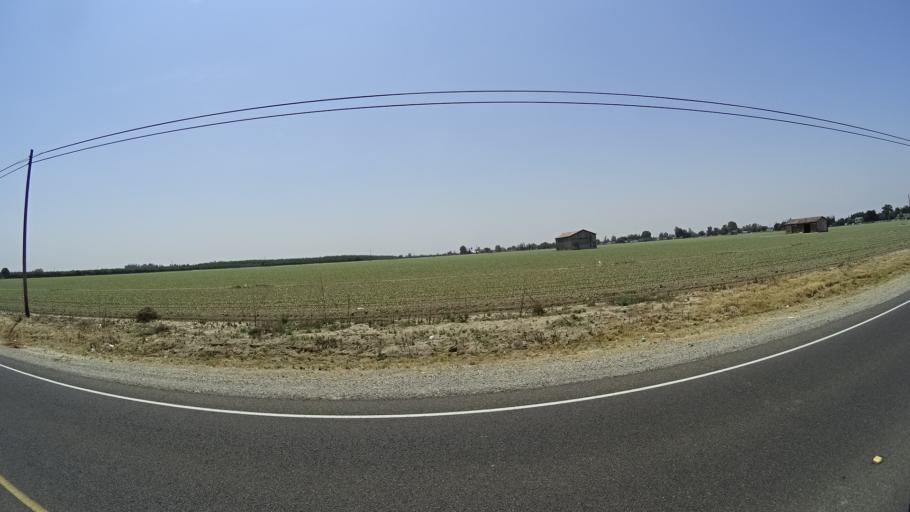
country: US
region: California
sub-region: Kings County
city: Lemoore
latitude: 36.3136
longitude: -119.7577
